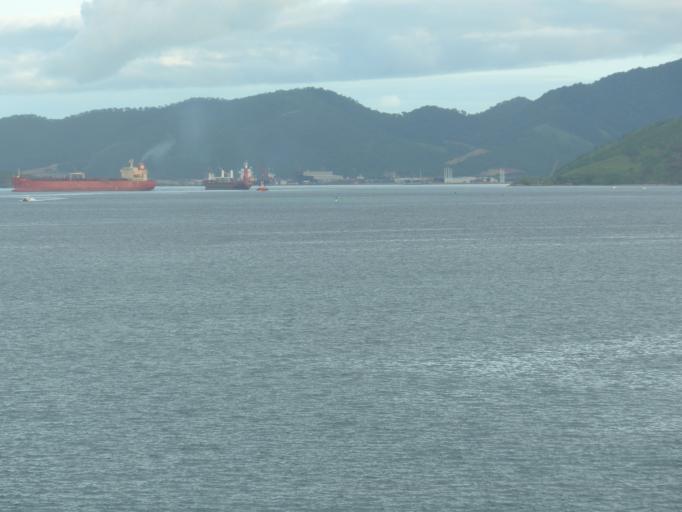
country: PG
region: National Capital
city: Port Moresby
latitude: -9.4743
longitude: 147.1497
